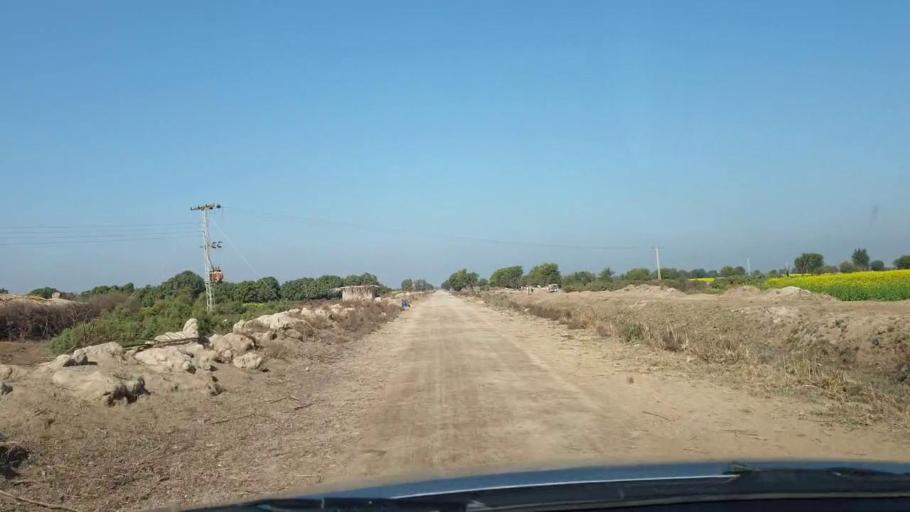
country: PK
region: Sindh
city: Jhol
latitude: 25.8816
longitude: 68.9022
